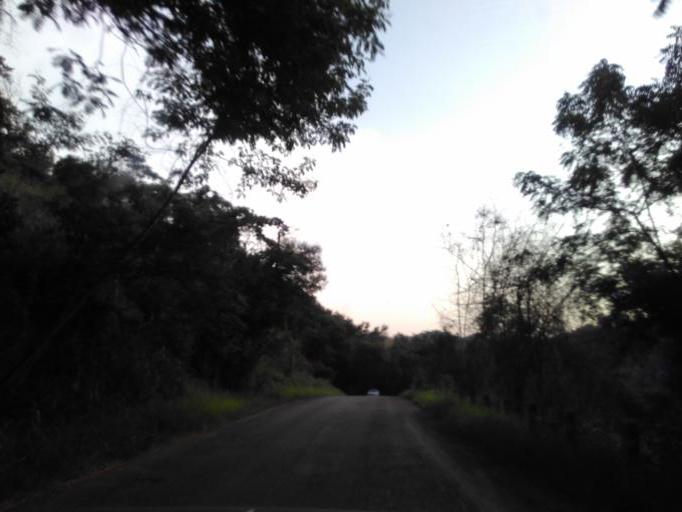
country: GH
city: Bekwai
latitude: 6.5436
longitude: -1.4286
